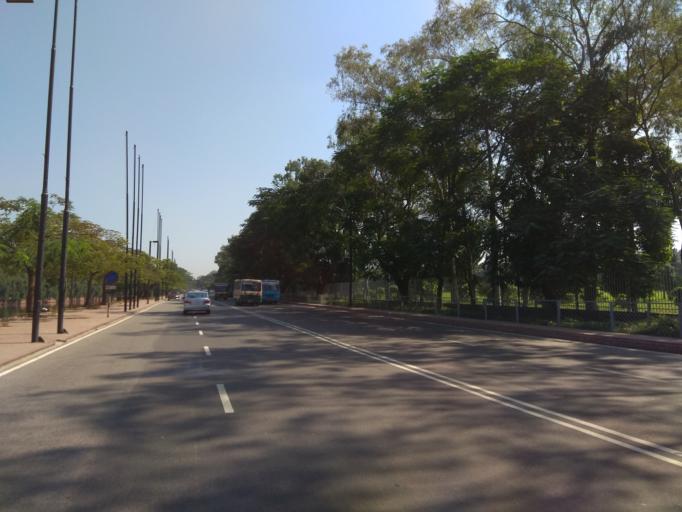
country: BD
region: Dhaka
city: Azimpur
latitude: 23.7648
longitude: 90.3784
